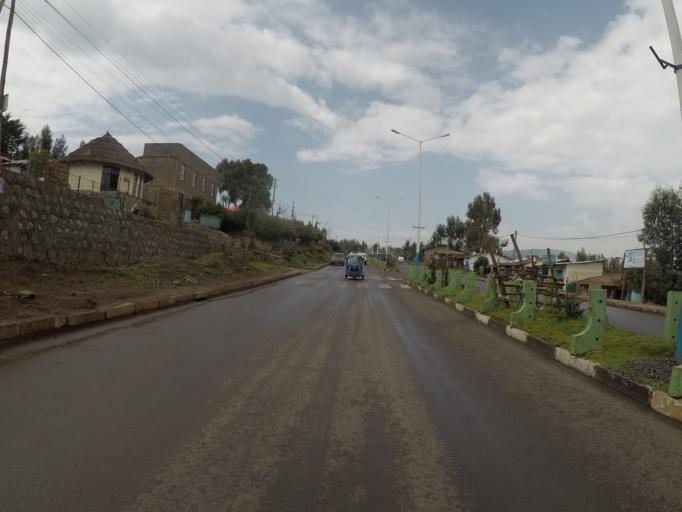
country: ET
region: Amhara
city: Debark'
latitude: 13.1491
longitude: 37.8948
